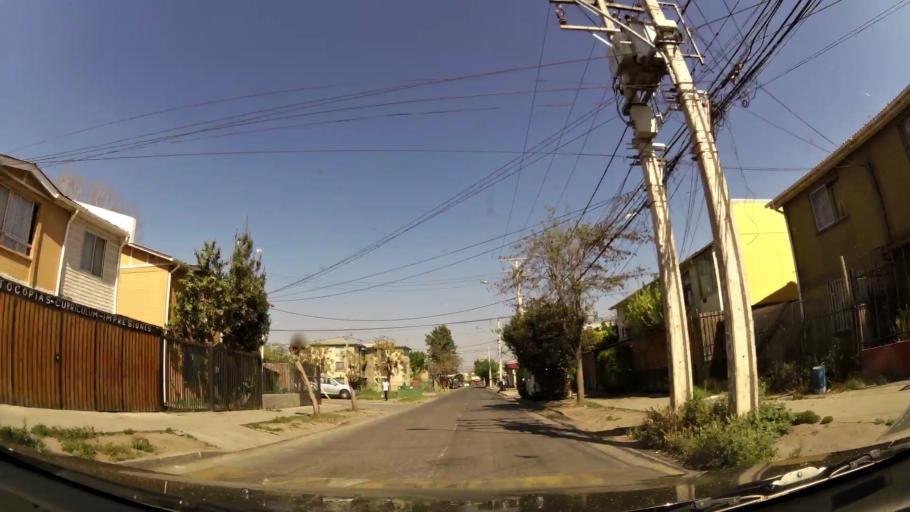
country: CL
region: Santiago Metropolitan
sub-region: Provincia de Santiago
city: Lo Prado
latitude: -33.3527
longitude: -70.7470
